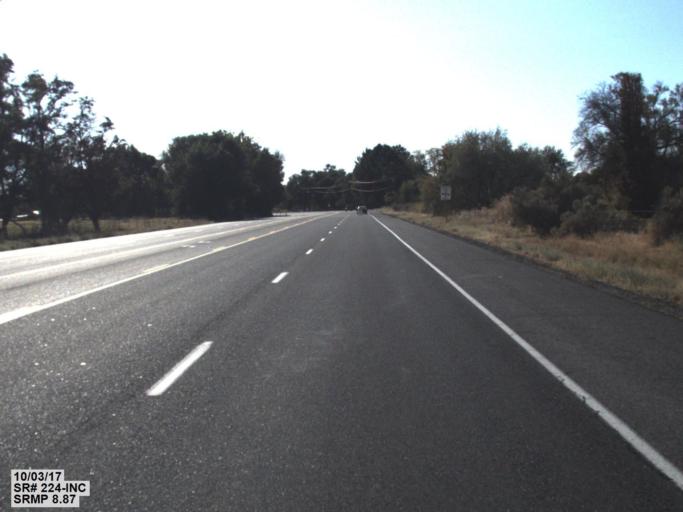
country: US
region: Washington
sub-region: Benton County
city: West Richland
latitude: 46.2964
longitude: -119.3247
